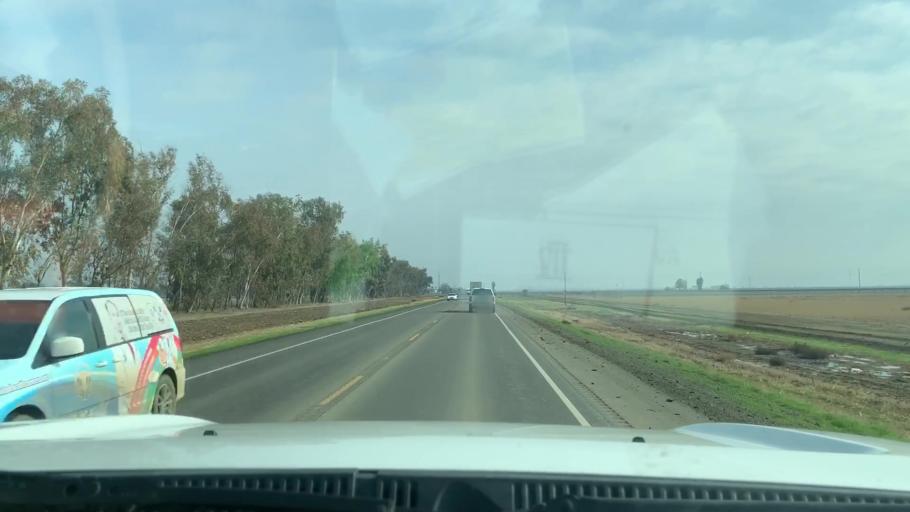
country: US
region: California
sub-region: Kings County
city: Lemoore Station
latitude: 36.2552
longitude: -119.9130
